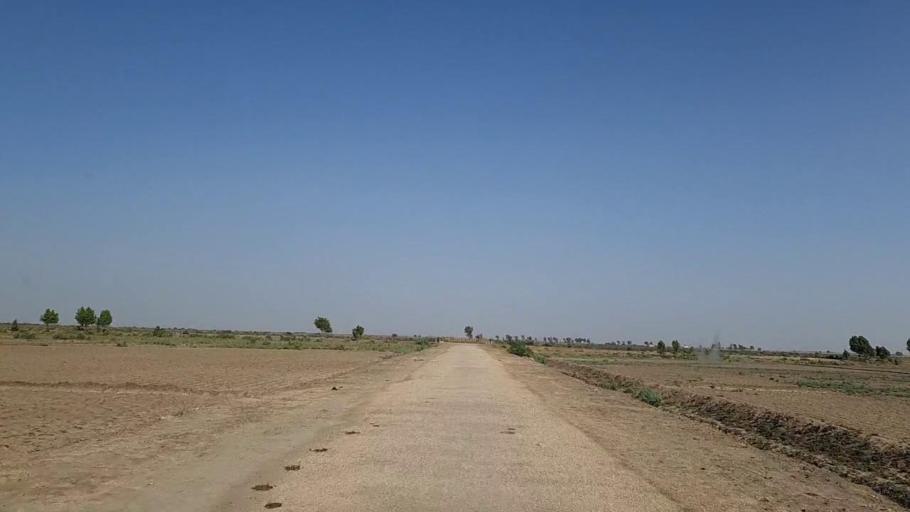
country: PK
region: Sindh
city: Jati
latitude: 24.5127
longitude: 68.2056
